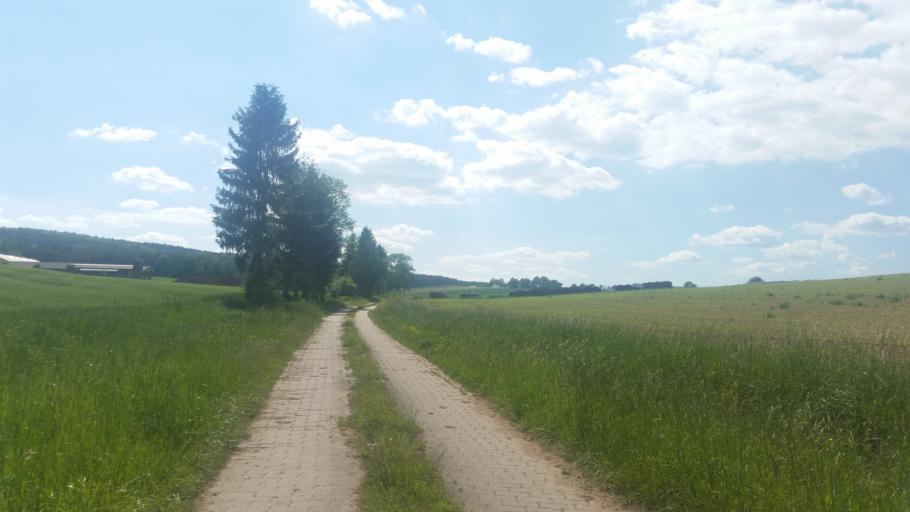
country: DE
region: Bavaria
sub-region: Regierungsbezirk Unterfranken
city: Burgpreppach
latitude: 50.1150
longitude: 10.6762
